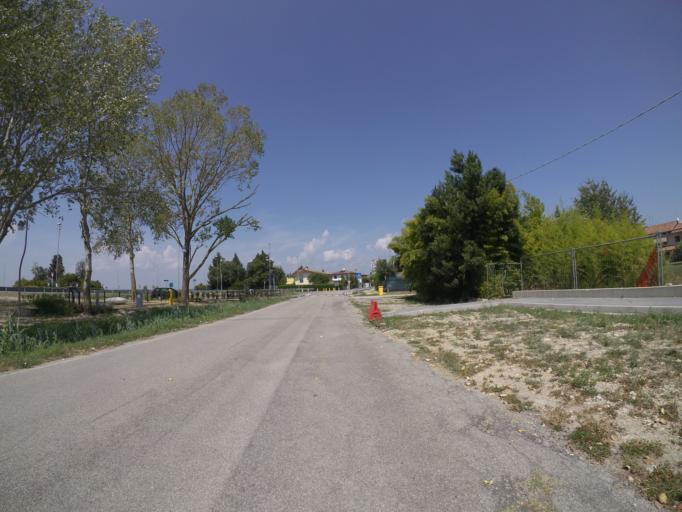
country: IT
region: Veneto
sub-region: Provincia di Venezia
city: Bibione
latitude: 45.6622
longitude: 13.0588
